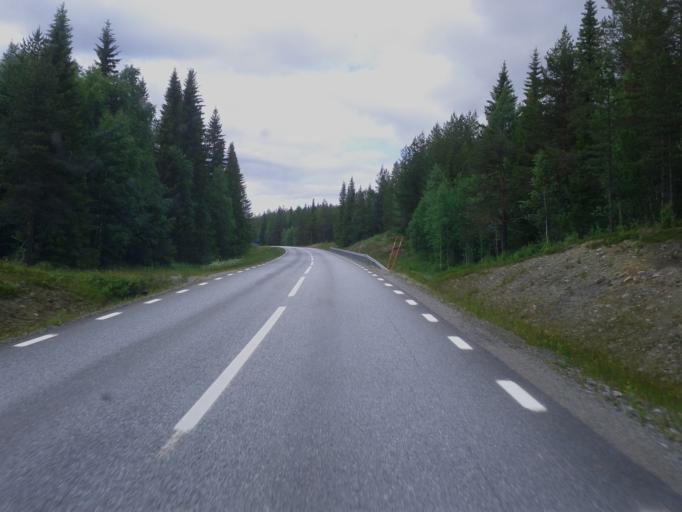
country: SE
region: Vaesterbotten
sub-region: Storumans Kommun
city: Fristad
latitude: 65.3968
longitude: 16.4433
